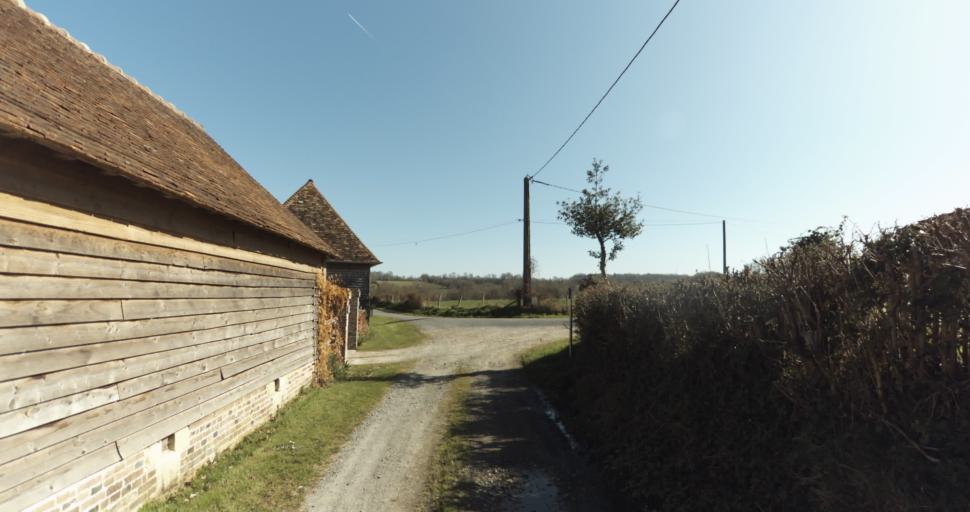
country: FR
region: Lower Normandy
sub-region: Departement du Calvados
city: Livarot
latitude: 48.9876
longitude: 0.0687
